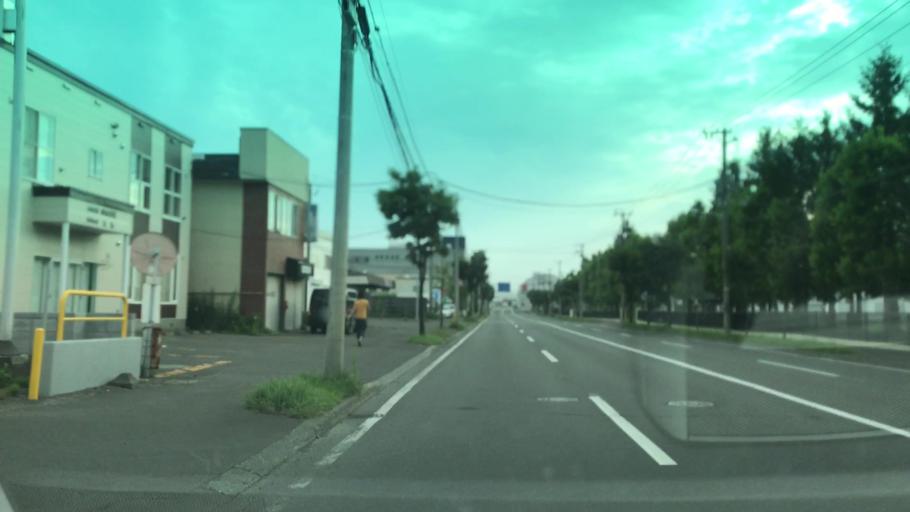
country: JP
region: Hokkaido
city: Sapporo
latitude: 43.0973
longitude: 141.3073
